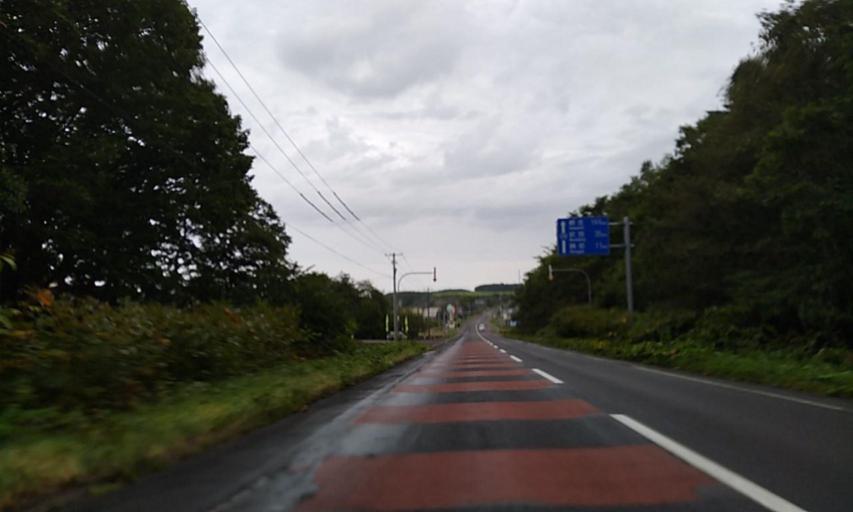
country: JP
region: Hokkaido
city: Mombetsu
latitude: 44.5294
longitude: 143.0415
